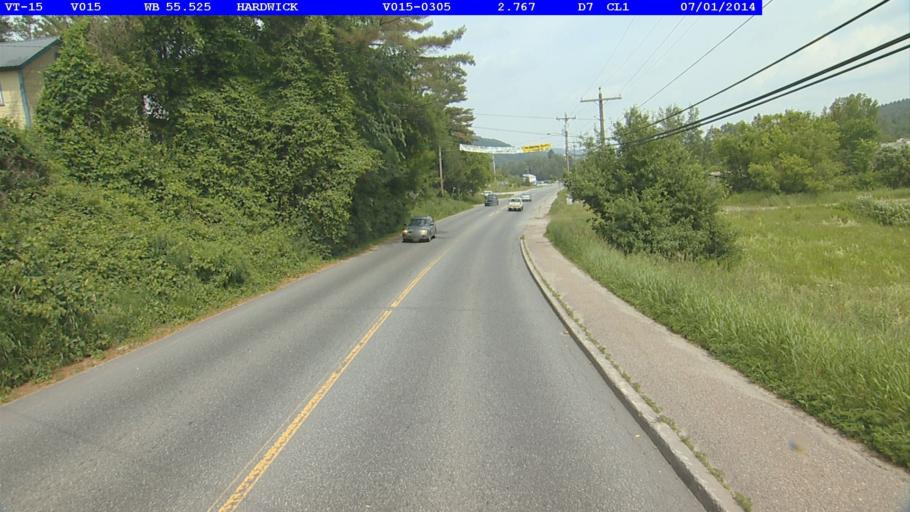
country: US
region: Vermont
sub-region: Caledonia County
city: Hardwick
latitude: 44.5114
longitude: -72.3734
